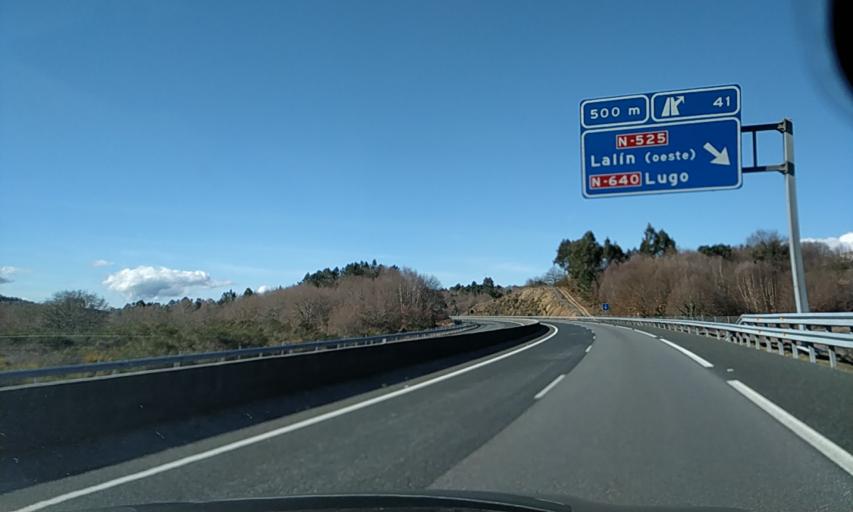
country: ES
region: Galicia
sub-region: Provincia de Pontevedra
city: Lalin
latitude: 42.6690
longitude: -8.1495
